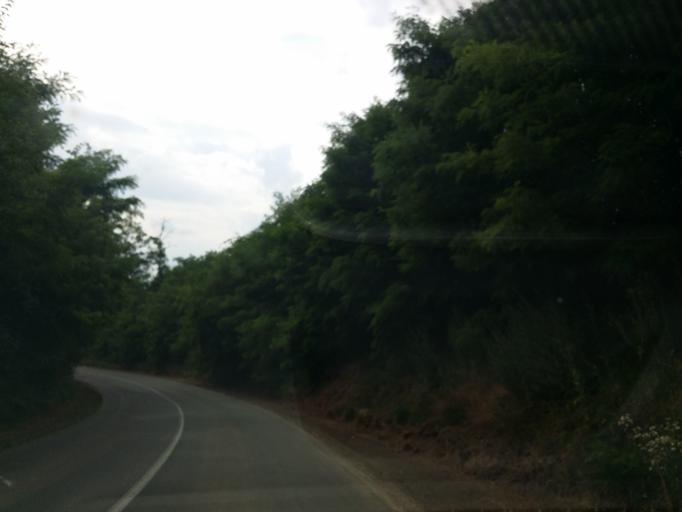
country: HU
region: Nograd
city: Bercel
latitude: 47.9792
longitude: 19.3827
